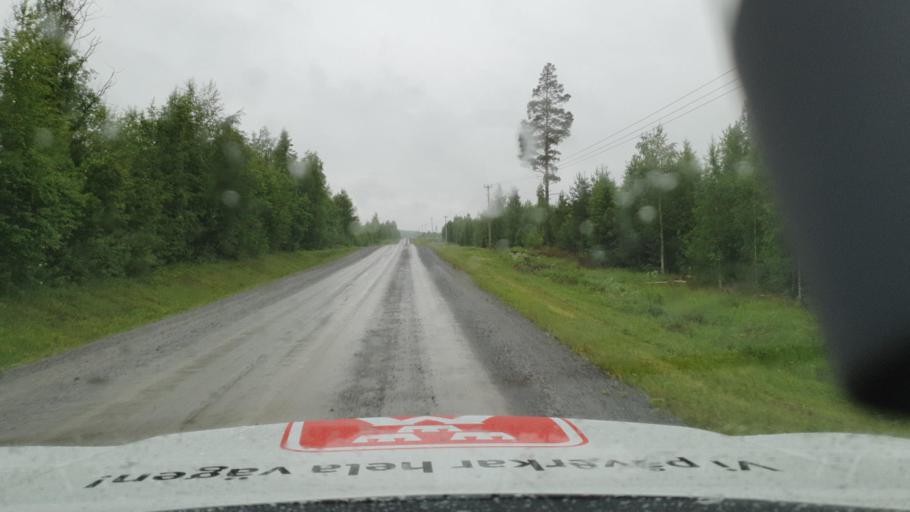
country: SE
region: Vaesterbotten
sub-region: Bjurholms Kommun
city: Bjurholm
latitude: 63.8786
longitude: 19.4428
